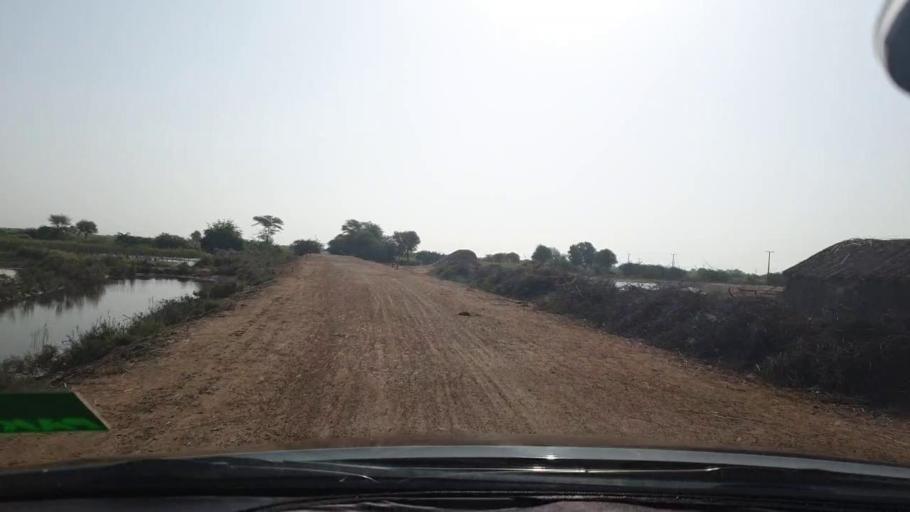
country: PK
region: Sindh
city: Tando Bago
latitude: 24.7190
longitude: 68.9615
